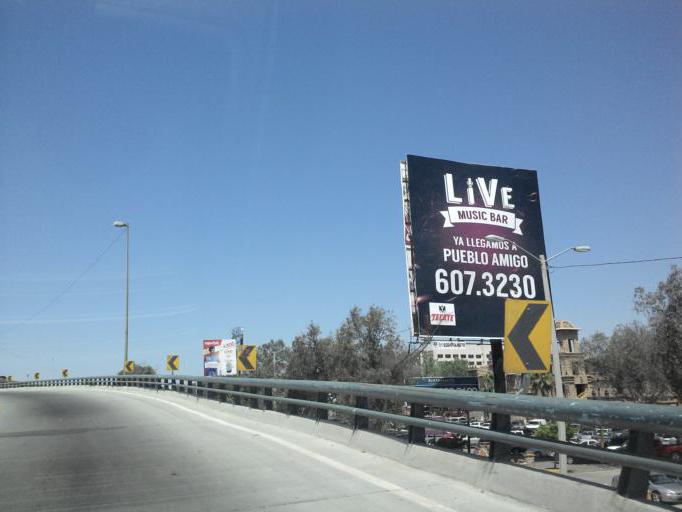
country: MX
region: Baja California
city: Tijuana
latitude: 32.5345
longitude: -117.0250
